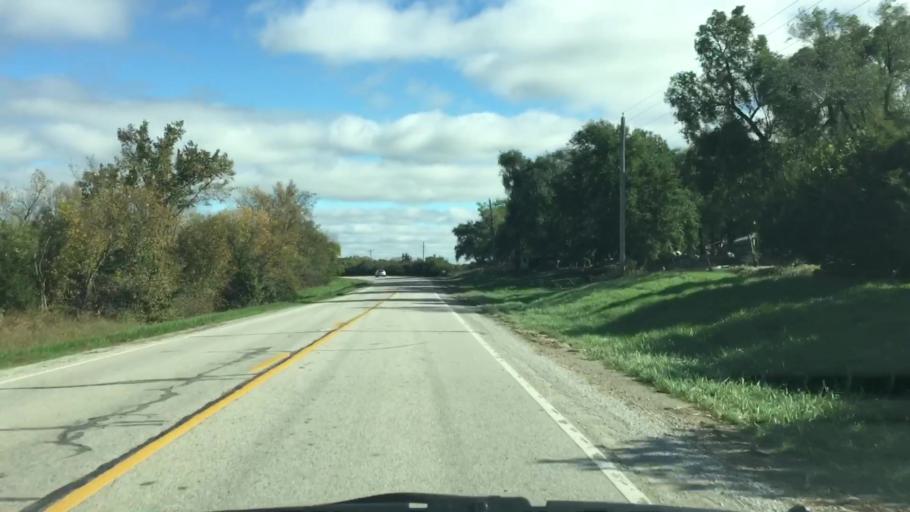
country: US
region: Iowa
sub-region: Decatur County
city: Leon
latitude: 40.7026
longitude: -93.7679
